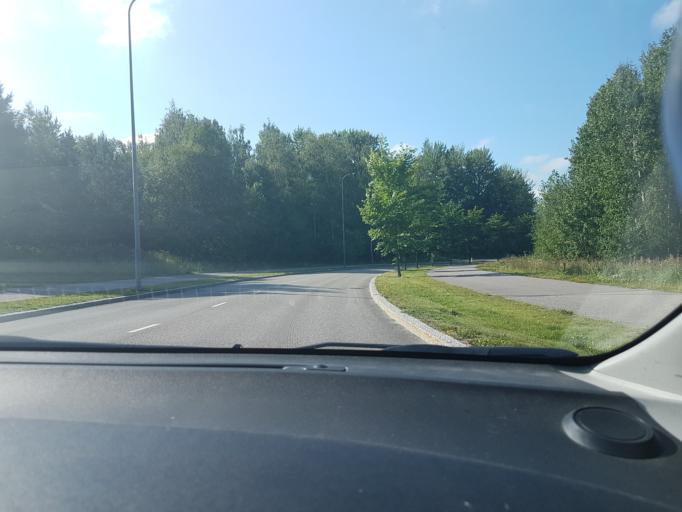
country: FI
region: Uusimaa
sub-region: Helsinki
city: Vantaa
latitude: 60.3325
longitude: 25.0277
